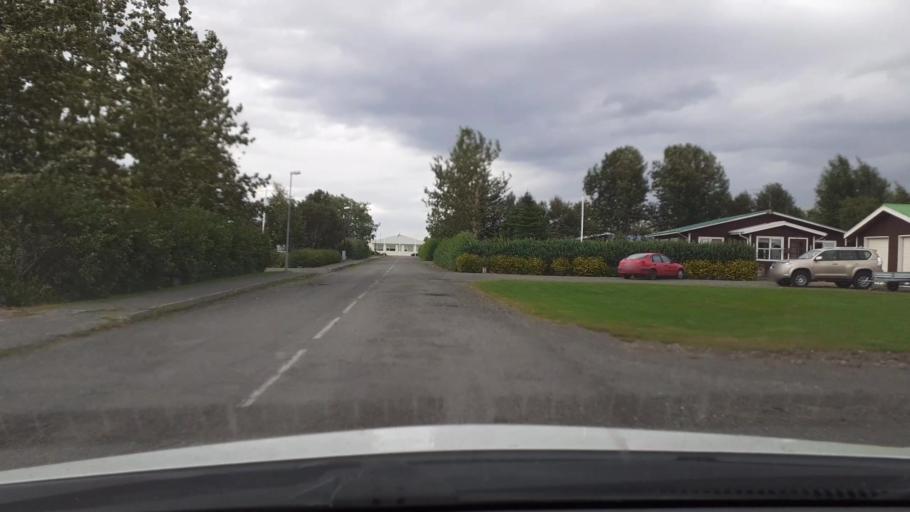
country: IS
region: West
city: Borgarnes
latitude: 64.5622
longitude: -21.7608
